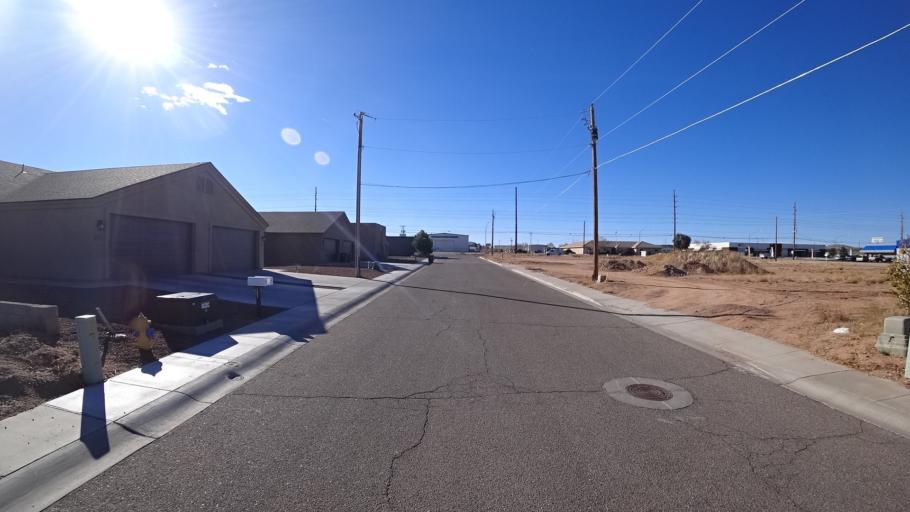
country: US
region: Arizona
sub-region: Mohave County
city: New Kingman-Butler
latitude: 35.2258
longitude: -114.0199
